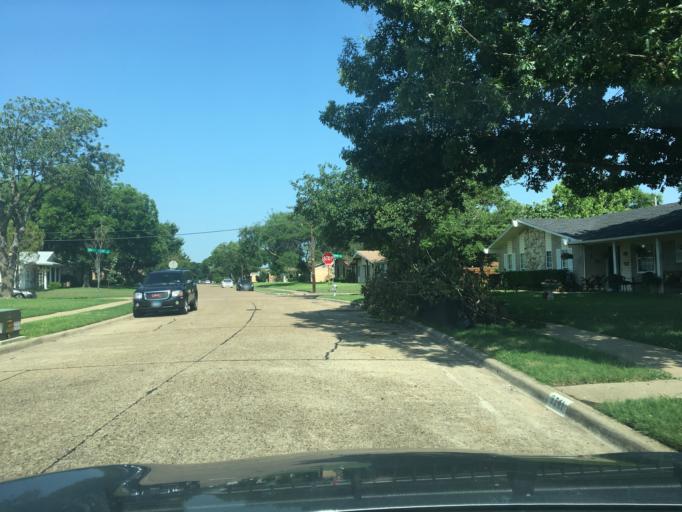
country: US
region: Texas
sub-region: Dallas County
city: Richardson
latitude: 32.9252
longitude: -96.6878
